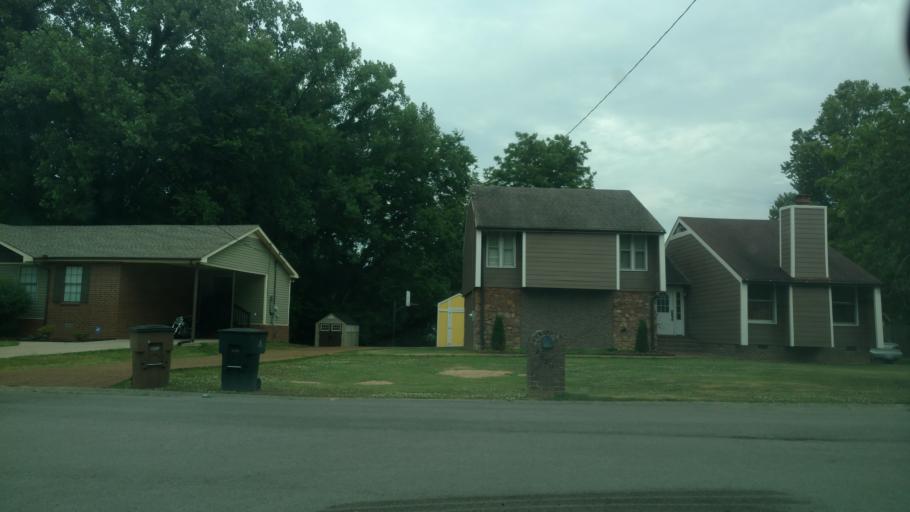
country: US
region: Tennessee
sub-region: Davidson County
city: Lakewood
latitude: 36.2028
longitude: -86.6996
